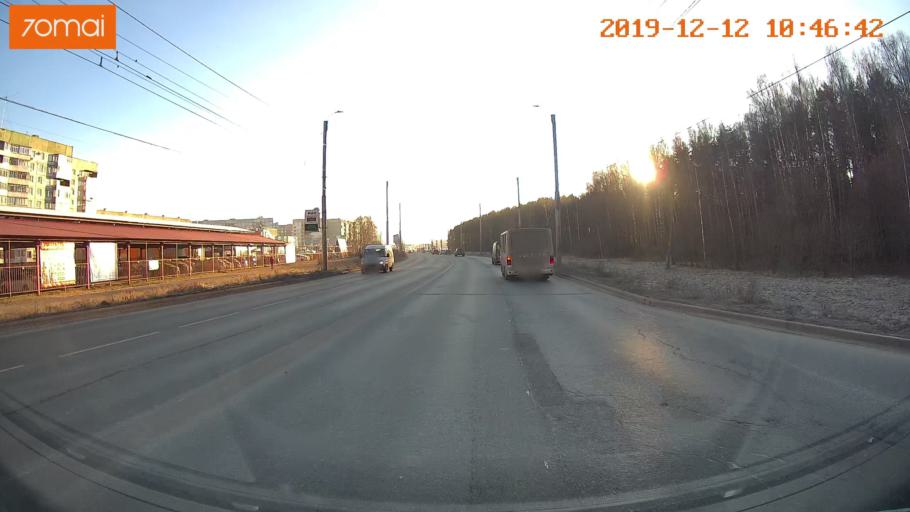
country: RU
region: Ivanovo
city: Kokhma
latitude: 56.9514
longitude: 41.0463
